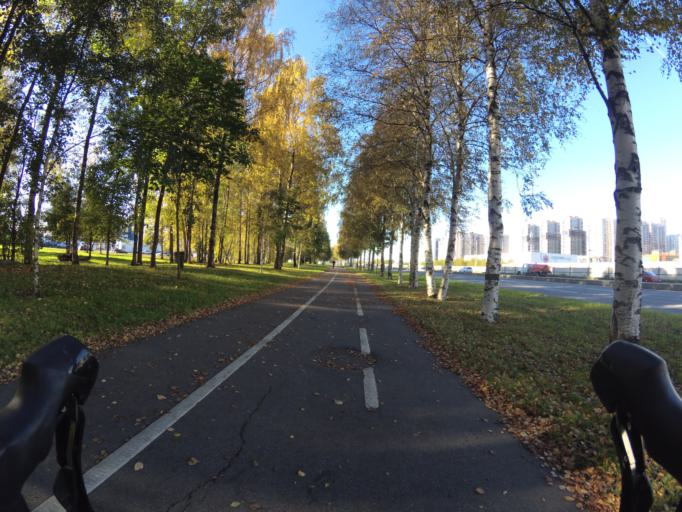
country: RU
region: Leningrad
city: Untolovo
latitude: 59.9940
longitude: 30.2084
